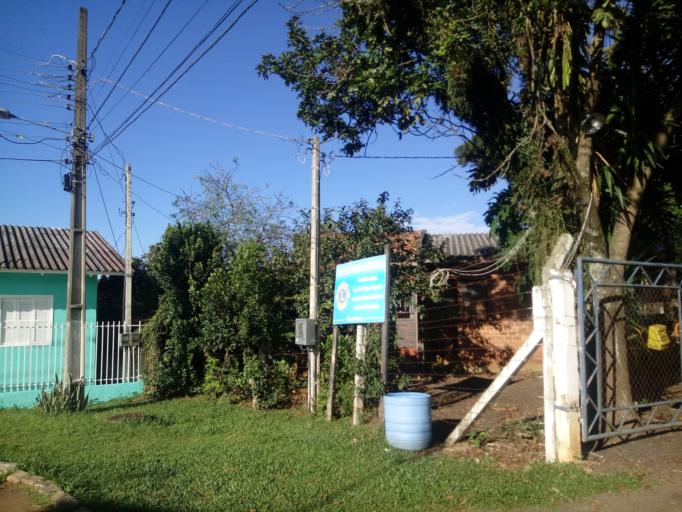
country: BR
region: Santa Catarina
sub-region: Chapeco
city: Chapeco
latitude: -27.1016
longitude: -52.6421
